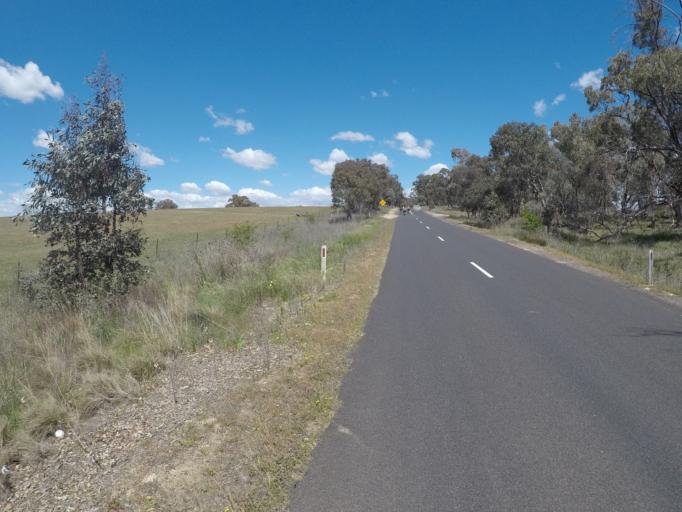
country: AU
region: New South Wales
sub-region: Bathurst Regional
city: Perthville
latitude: -33.5381
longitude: 149.4397
